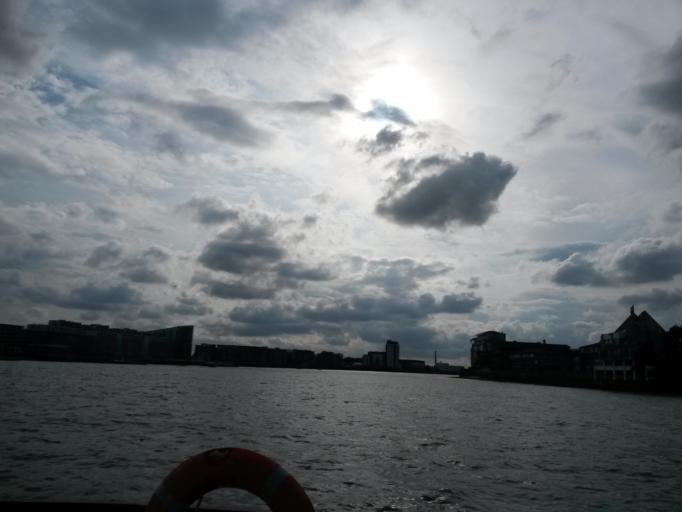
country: GB
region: England
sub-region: Greater London
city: Poplar
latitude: 51.4859
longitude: -0.0082
